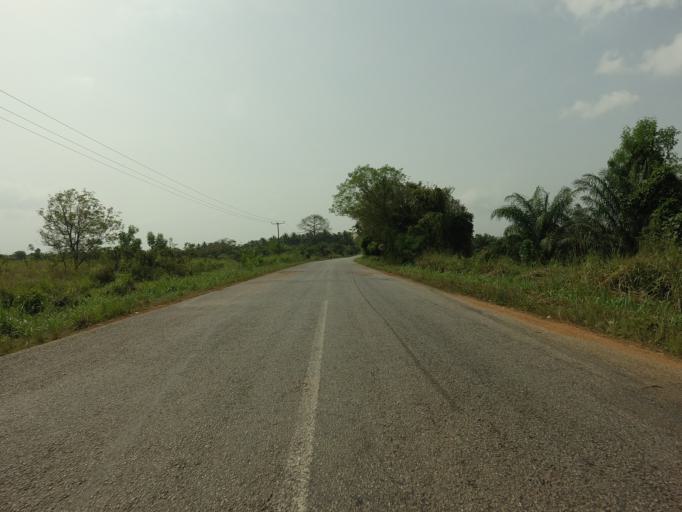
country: GH
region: Volta
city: Ho
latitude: 6.3224
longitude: 0.1629
